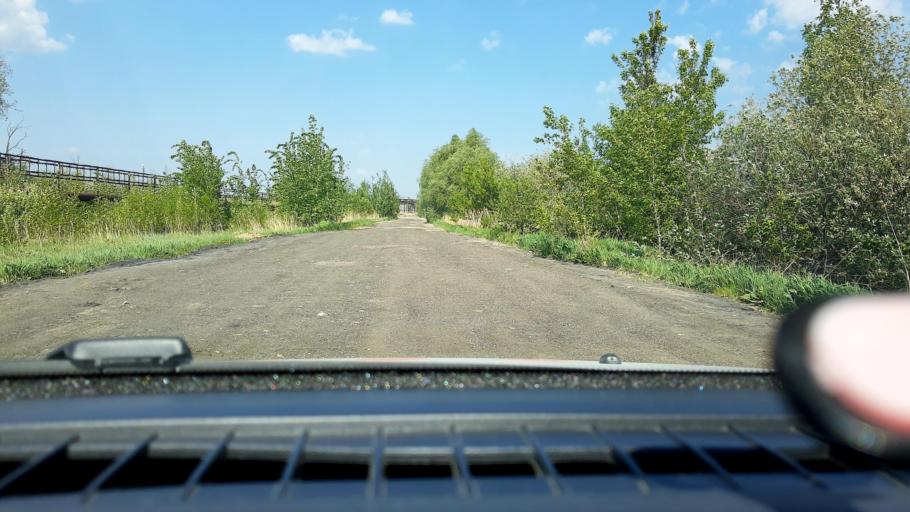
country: RU
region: Nizjnij Novgorod
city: Kstovo
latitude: 56.1314
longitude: 44.1275
